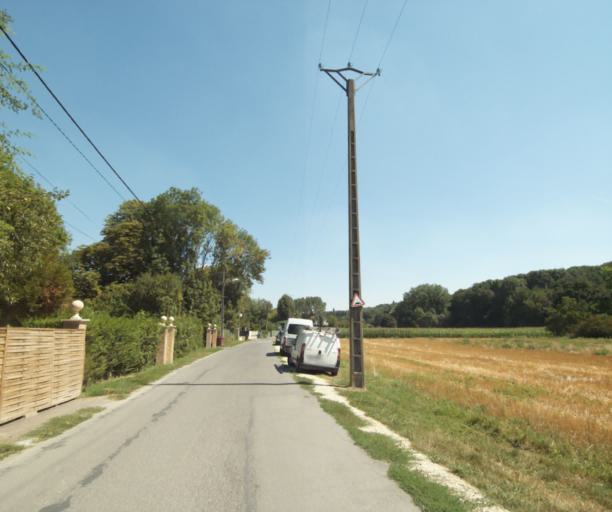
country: FR
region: Ile-de-France
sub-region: Departement de Seine-et-Marne
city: Dampmart
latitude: 48.8817
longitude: 2.7356
